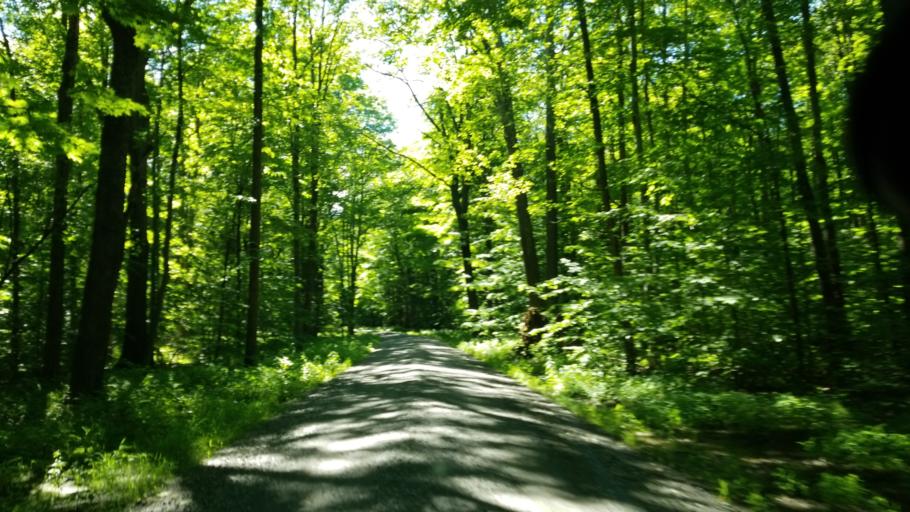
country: US
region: Pennsylvania
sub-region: Clearfield County
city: Clearfield
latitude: 41.2083
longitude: -78.4099
